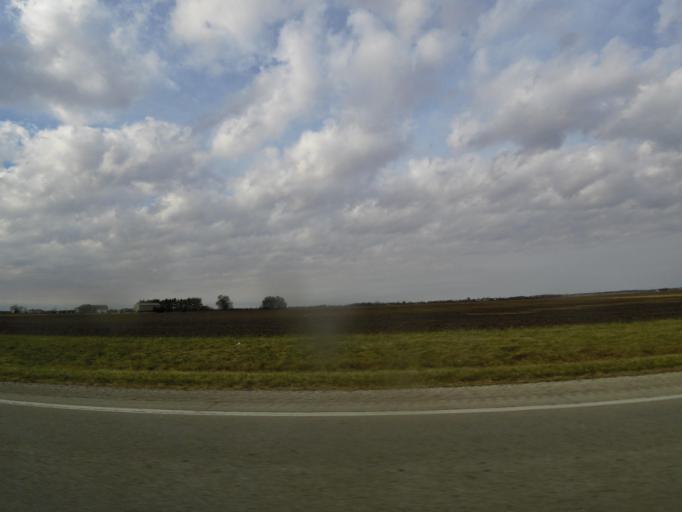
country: US
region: Illinois
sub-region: Christian County
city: Pana
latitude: 39.3395
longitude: -89.0813
